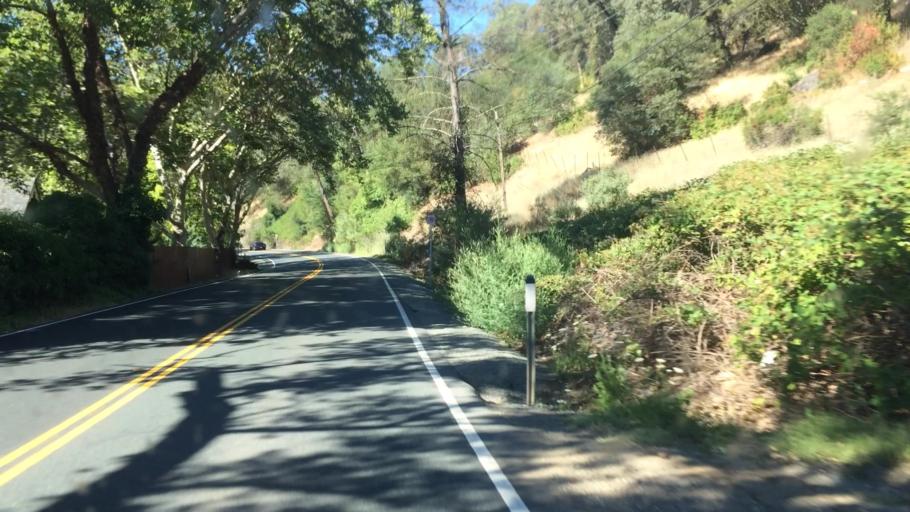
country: US
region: California
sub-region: Amador County
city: Plymouth
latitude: 38.5534
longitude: -120.8490
